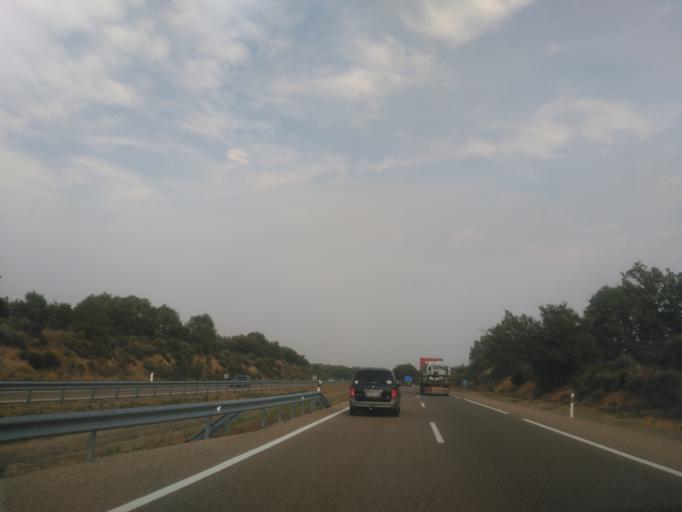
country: ES
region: Castille and Leon
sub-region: Provincia de Zamora
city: Mombuey
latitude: 42.0180
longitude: -6.3418
